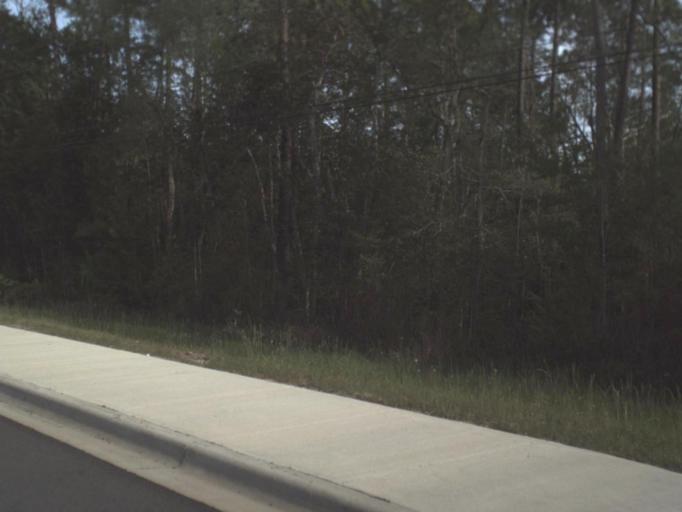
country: US
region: Florida
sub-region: Santa Rosa County
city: Holley
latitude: 30.4458
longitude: -86.8850
